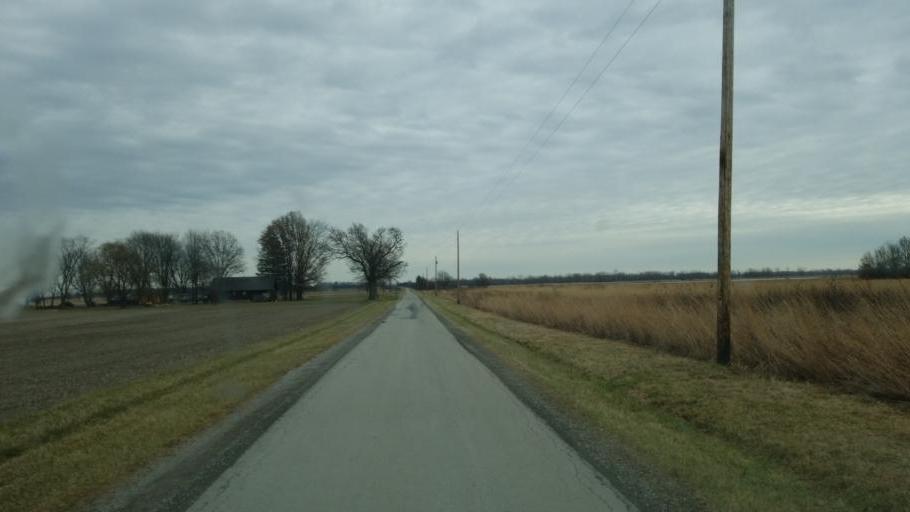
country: US
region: Ohio
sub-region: Wyandot County
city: Upper Sandusky
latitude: 40.7236
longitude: -83.3310
